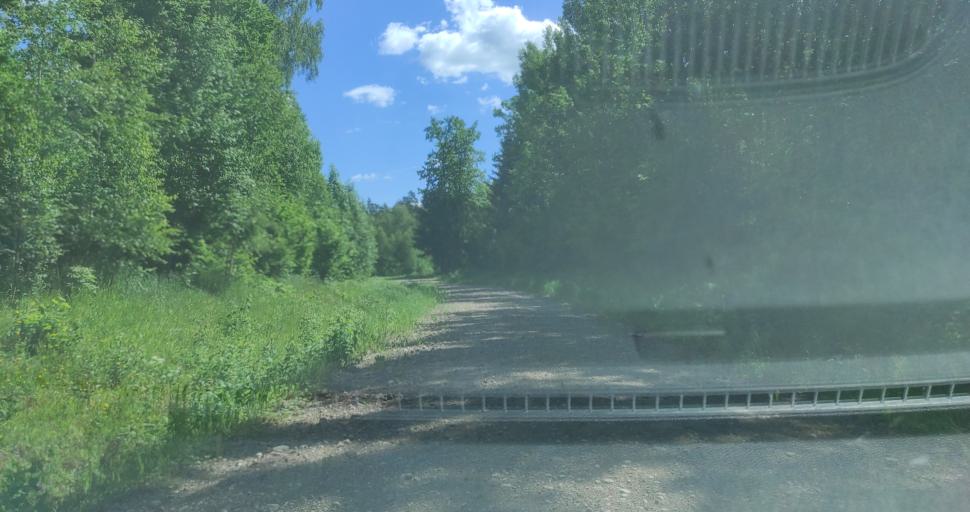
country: LV
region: Alsunga
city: Alsunga
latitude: 56.8866
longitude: 21.7258
